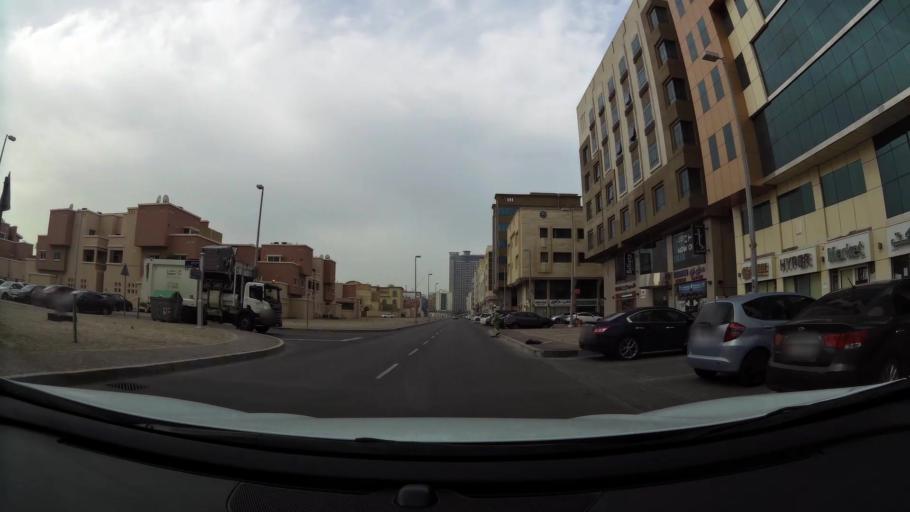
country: AE
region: Abu Dhabi
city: Abu Dhabi
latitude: 24.4759
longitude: 54.3819
